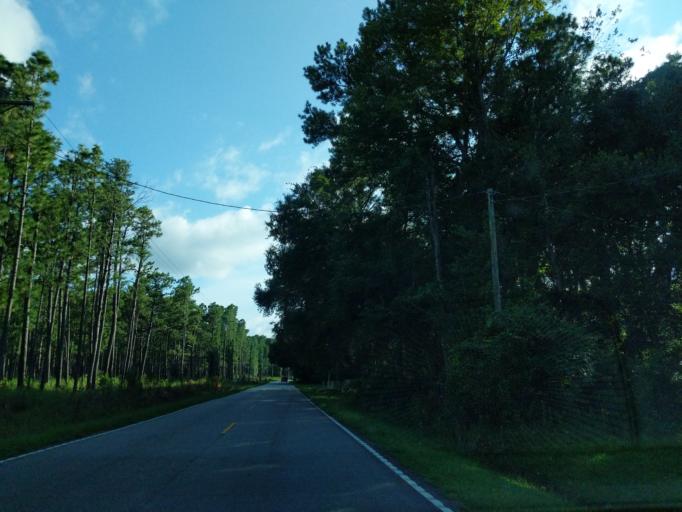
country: US
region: South Carolina
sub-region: Charleston County
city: Awendaw
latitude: 33.1429
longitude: -79.4204
